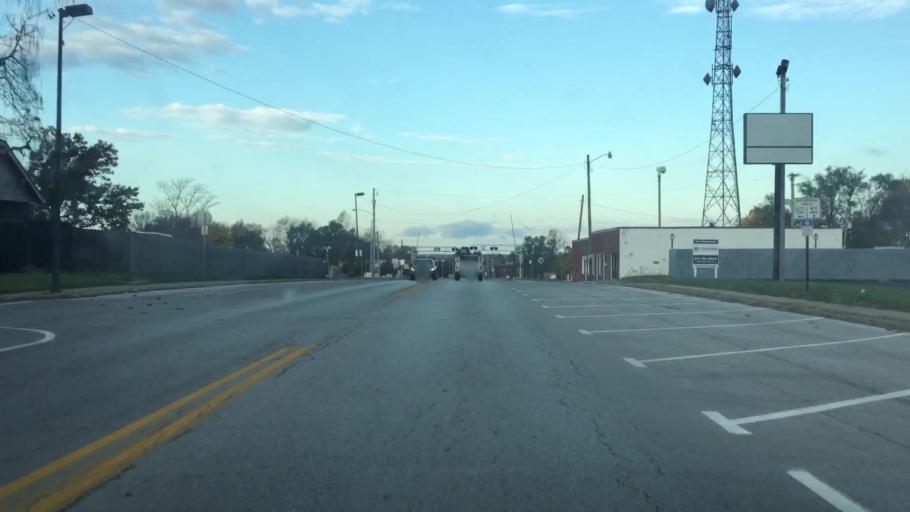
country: US
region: Missouri
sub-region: Jackson County
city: Grandview
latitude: 38.8896
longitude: -94.5384
